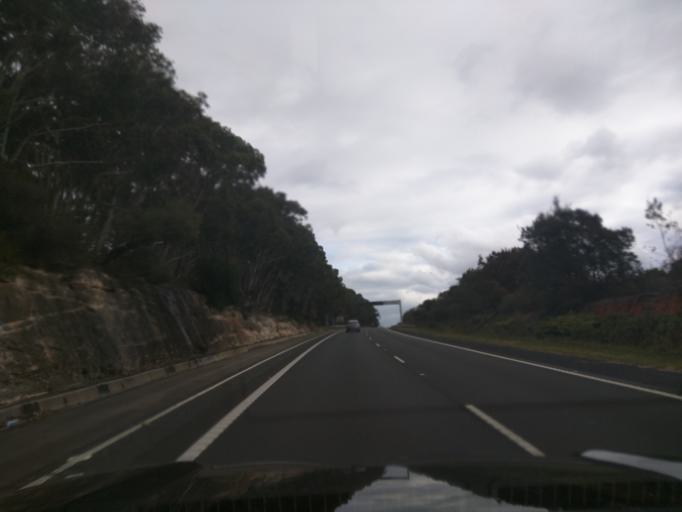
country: AU
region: New South Wales
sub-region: Wollongong
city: Helensburgh
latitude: -34.2435
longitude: 150.9425
